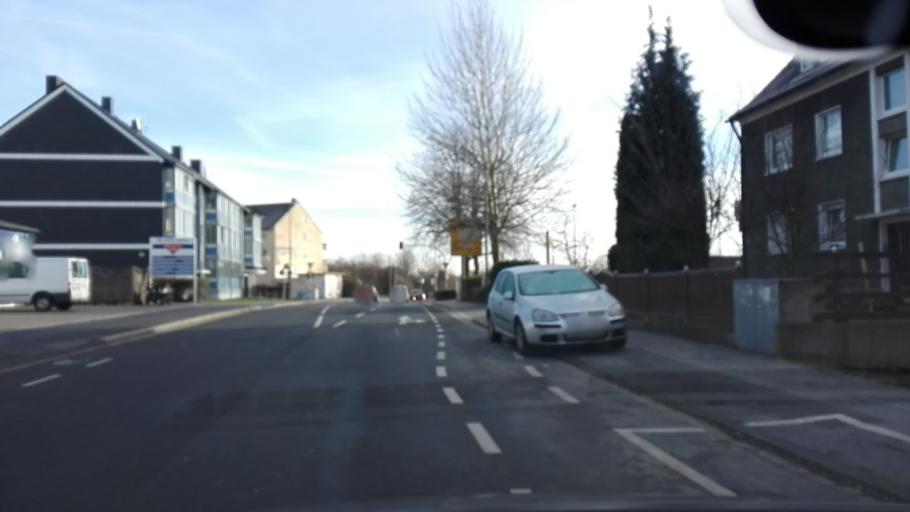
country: DE
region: North Rhine-Westphalia
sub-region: Regierungsbezirk Arnsberg
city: Dortmund
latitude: 51.5080
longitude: 7.4206
